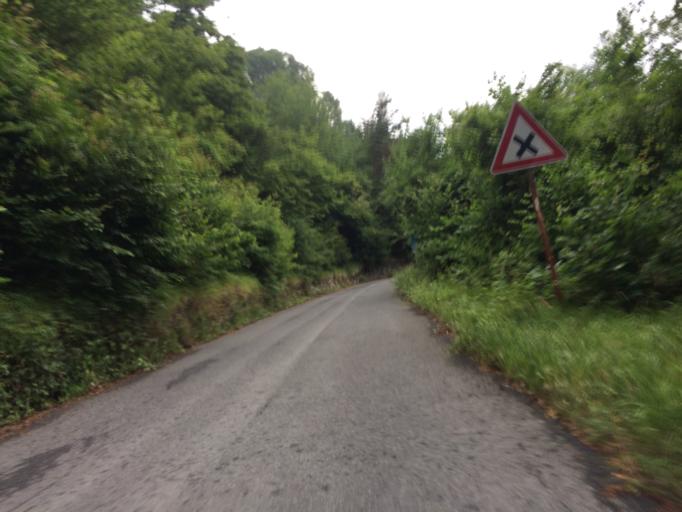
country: IT
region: Liguria
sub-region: Provincia di Imperia
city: Triora
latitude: 43.9680
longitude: 7.7390
